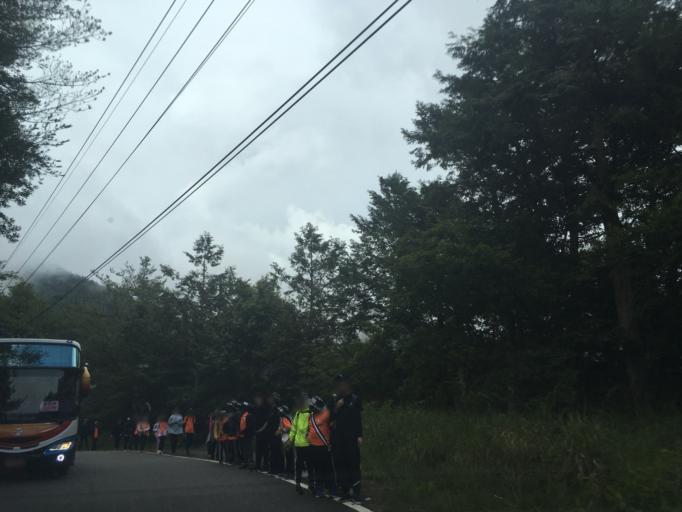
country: TW
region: Taiwan
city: Fengyuan
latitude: 24.2677
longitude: 121.0218
